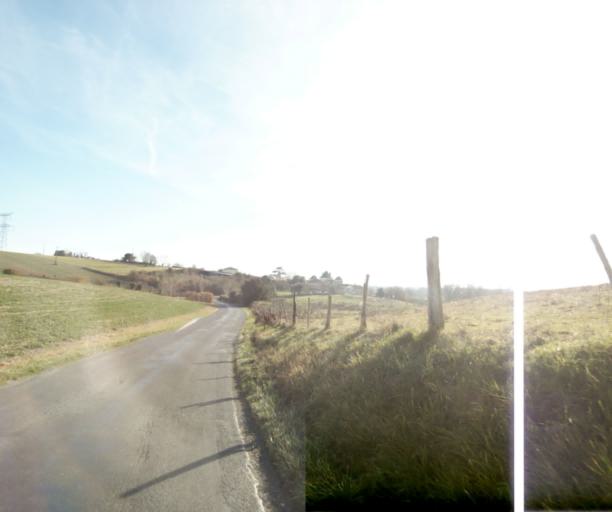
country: FR
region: Poitou-Charentes
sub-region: Departement de la Charente-Maritime
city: Les Gonds
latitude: 45.7308
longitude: -0.5872
